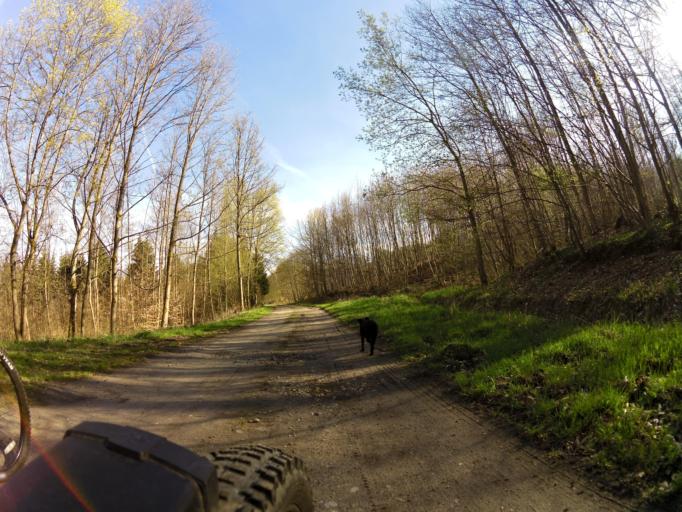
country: PL
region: West Pomeranian Voivodeship
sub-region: Powiat lobeski
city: Lobez
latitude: 53.7642
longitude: 15.5874
